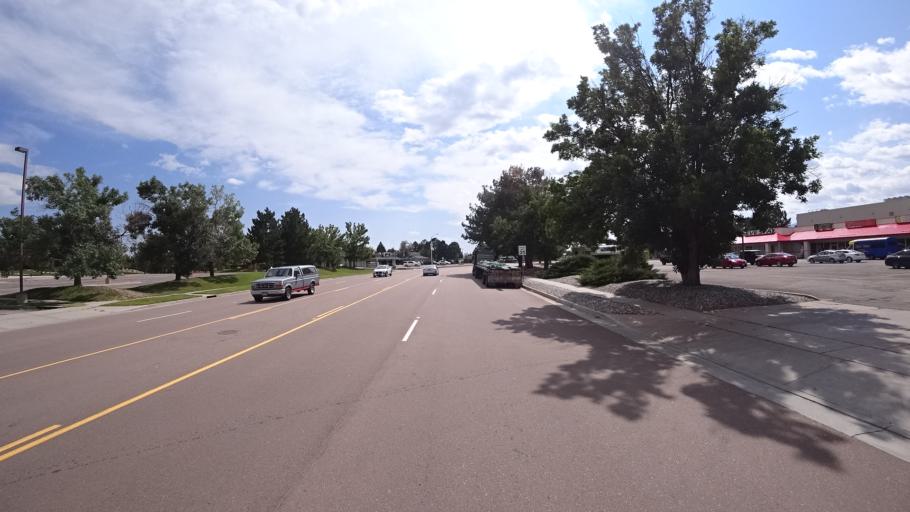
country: US
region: Colorado
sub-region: El Paso County
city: Cimarron Hills
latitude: 38.8811
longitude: -104.7537
